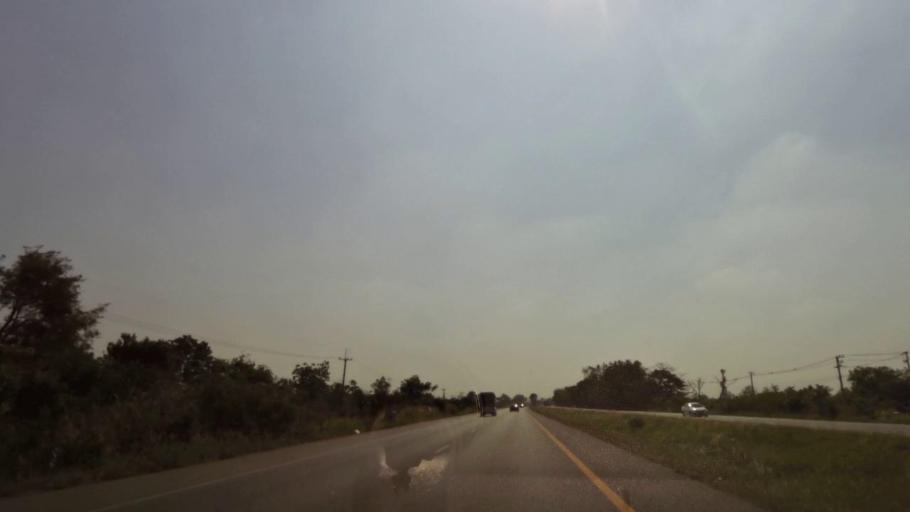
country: TH
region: Phichit
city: Wachira Barami
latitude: 16.4770
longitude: 100.1471
